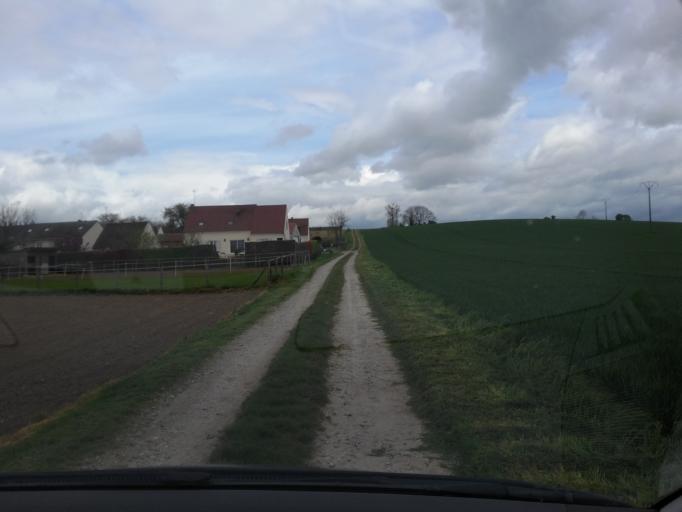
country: FR
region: Picardie
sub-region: Departement de l'Oise
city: Grandfresnoy
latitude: 49.3657
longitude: 2.6633
